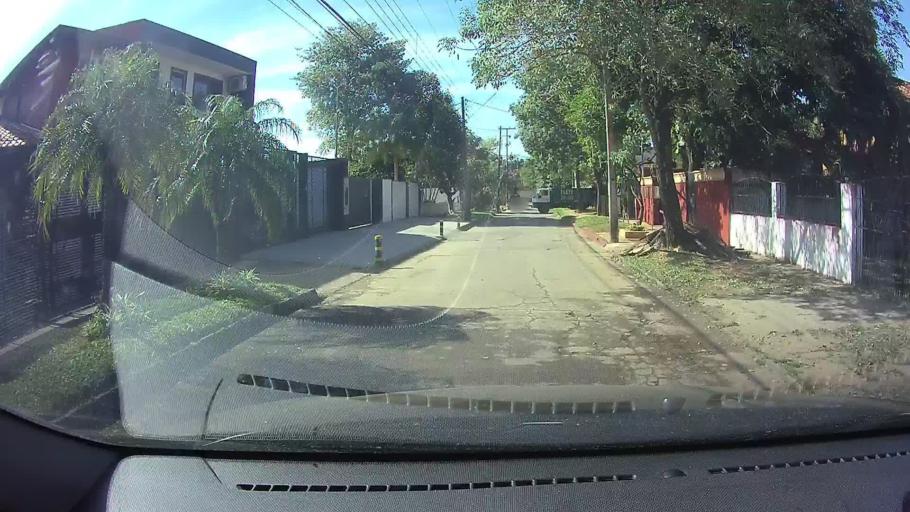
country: PY
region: Central
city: Fernando de la Mora
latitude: -25.2832
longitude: -57.5440
